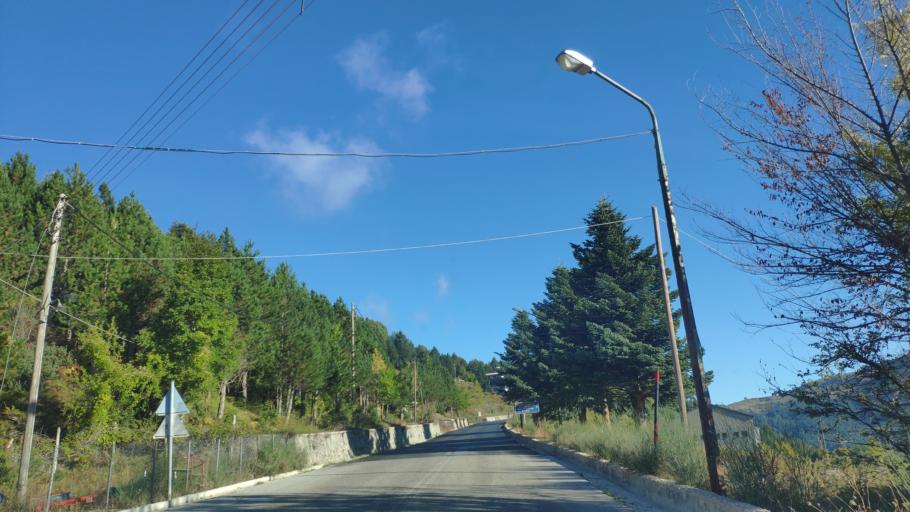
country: GR
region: Epirus
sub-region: Nomos Ioanninon
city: Metsovo
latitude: 39.7709
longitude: 21.1762
